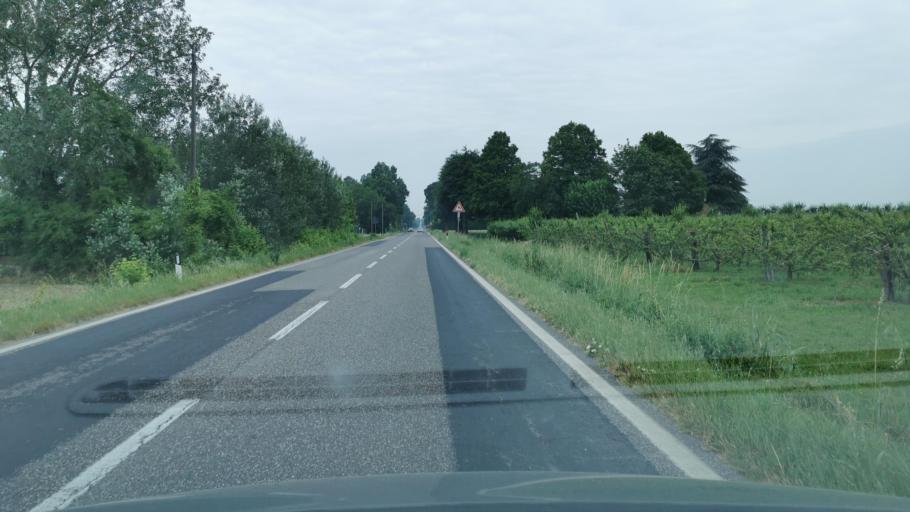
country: IT
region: Emilia-Romagna
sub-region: Provincia di Ravenna
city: Russi
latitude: 44.3932
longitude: 12.0436
